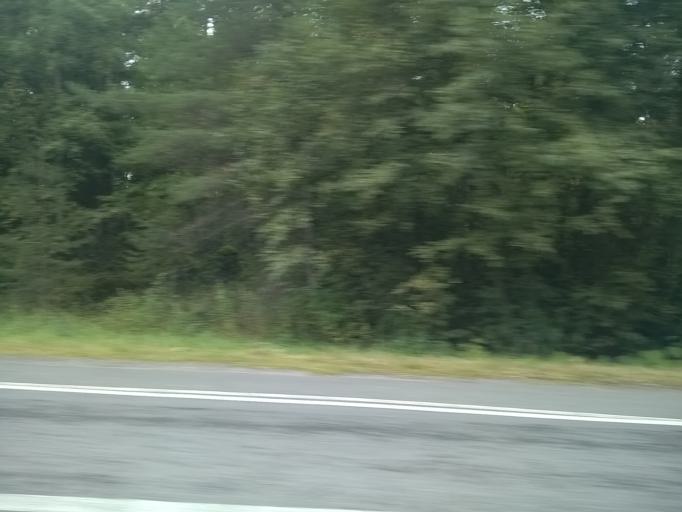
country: FI
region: Pirkanmaa
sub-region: Tampere
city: Tampere
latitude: 61.4647
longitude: 23.8419
